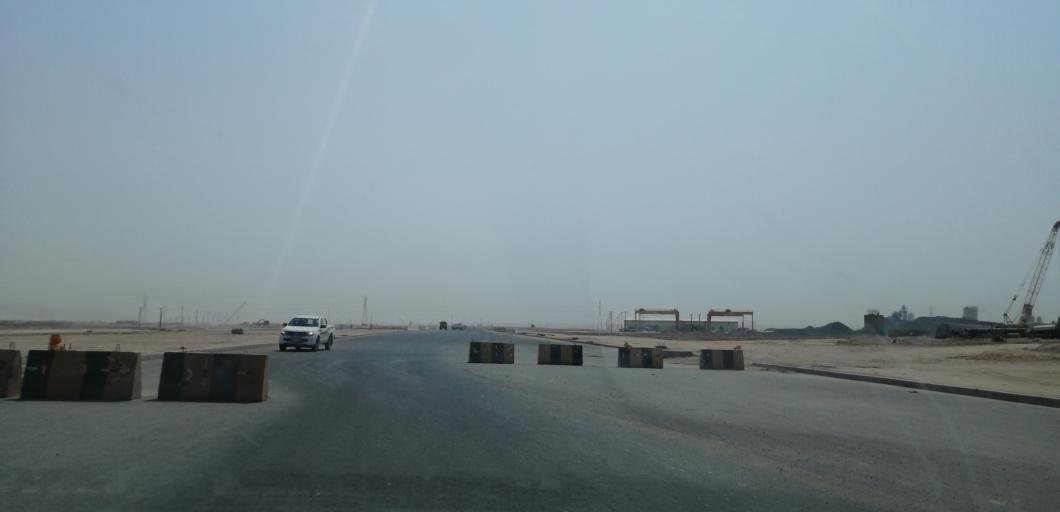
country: KW
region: Muhafazat al Jahra'
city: Al Jahra'
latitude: 29.4465
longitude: 47.6254
